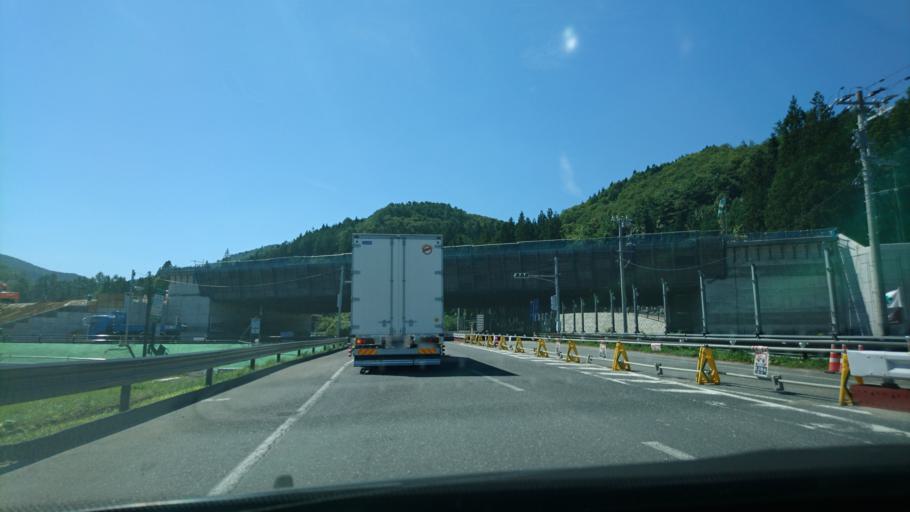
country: JP
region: Iwate
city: Tono
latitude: 39.2664
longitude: 141.5872
